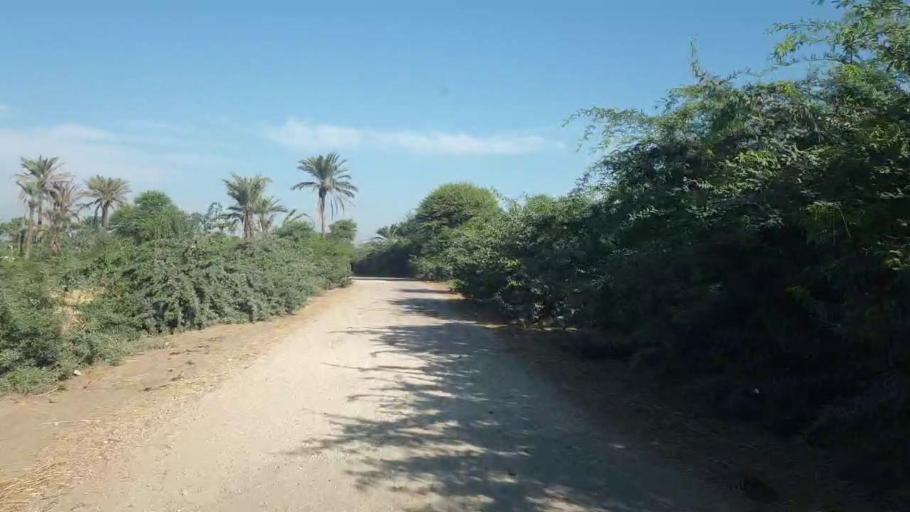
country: PK
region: Sindh
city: Talhar
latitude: 24.8955
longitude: 68.8122
